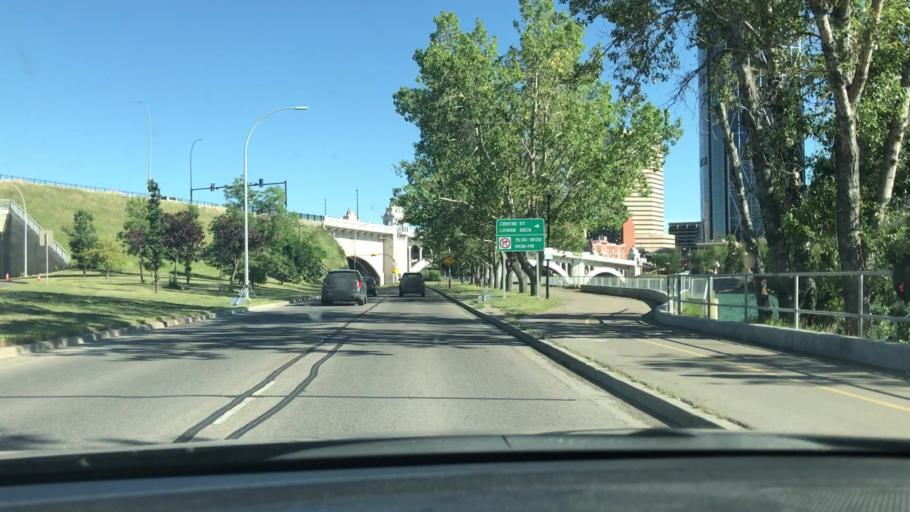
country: CA
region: Alberta
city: Calgary
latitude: 51.0551
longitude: -114.0640
